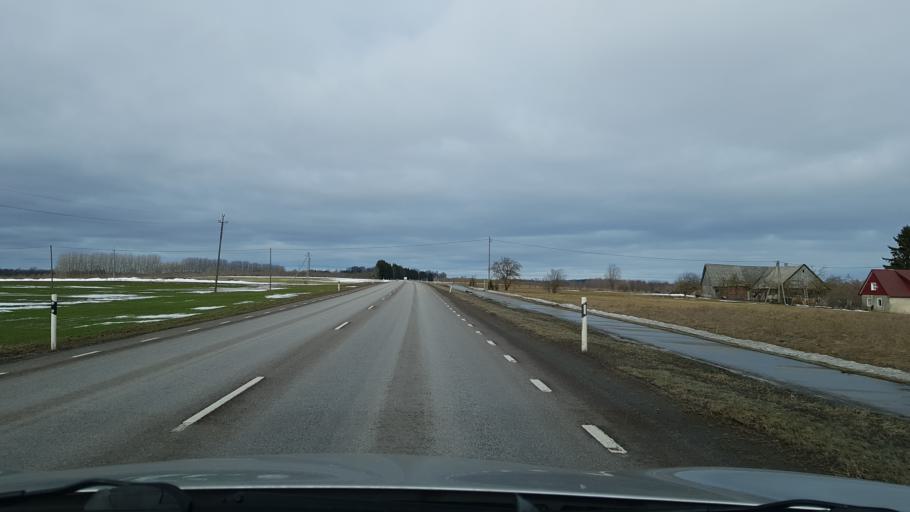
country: EE
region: Jogevamaa
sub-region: Tabivere vald
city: Tabivere
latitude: 58.5387
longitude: 26.6263
